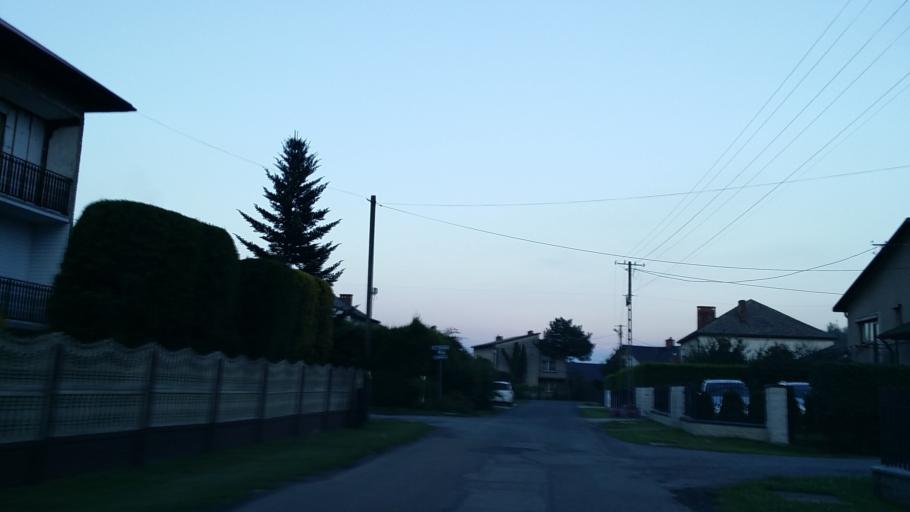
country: PL
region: Lesser Poland Voivodeship
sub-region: Powiat oswiecimski
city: Przeciszow
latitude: 50.0212
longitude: 19.3780
